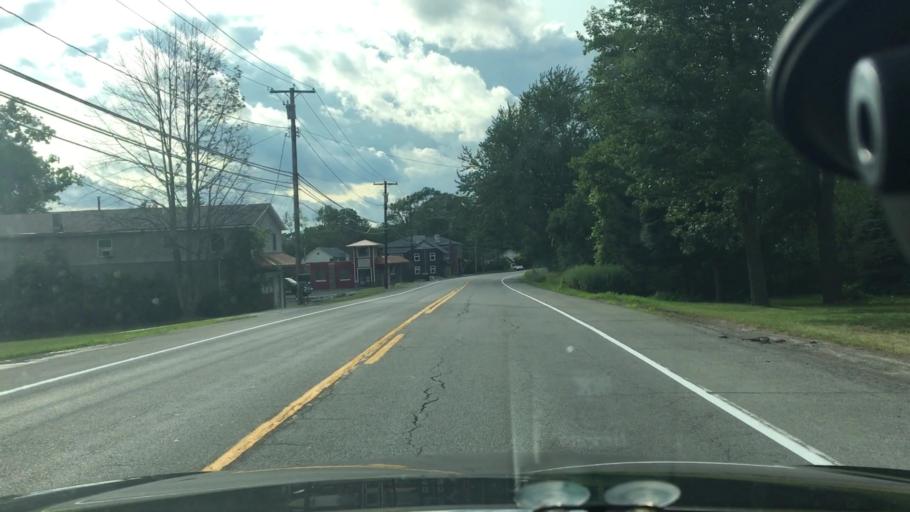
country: US
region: New York
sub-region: Erie County
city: Elma Center
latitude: 42.8185
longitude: -78.6763
